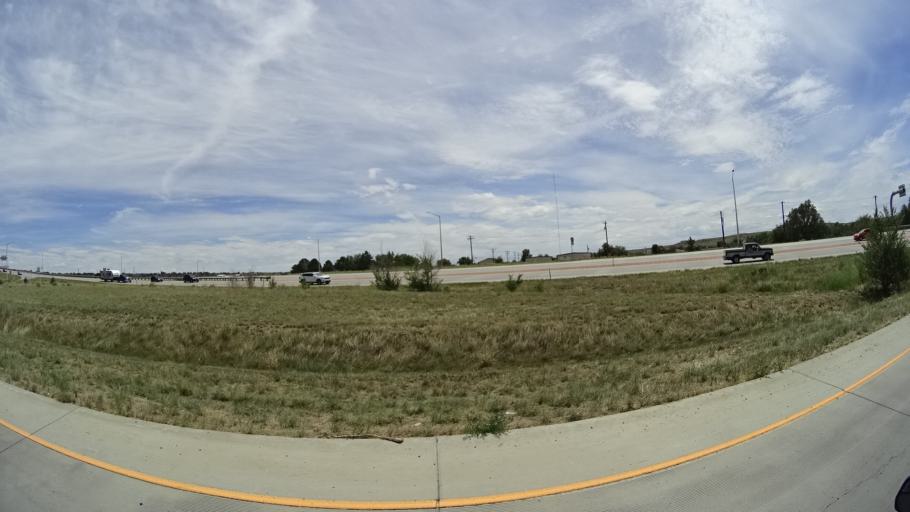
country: US
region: Colorado
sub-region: El Paso County
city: Security-Widefield
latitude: 38.7236
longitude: -104.7219
